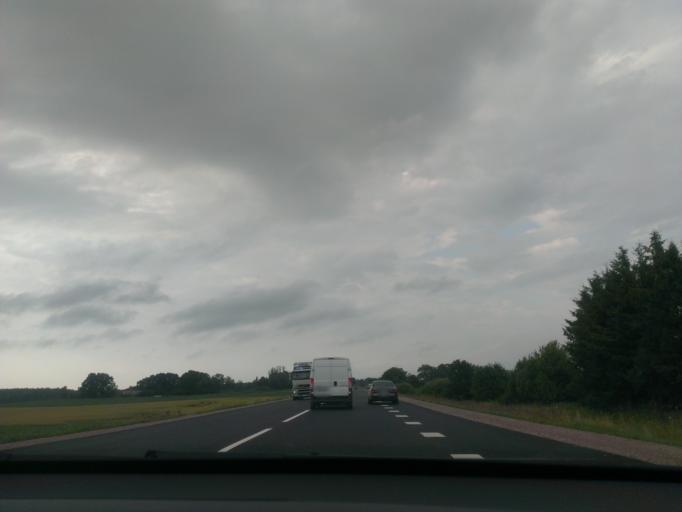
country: LV
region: Lecava
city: Iecava
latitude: 56.6151
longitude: 24.2161
